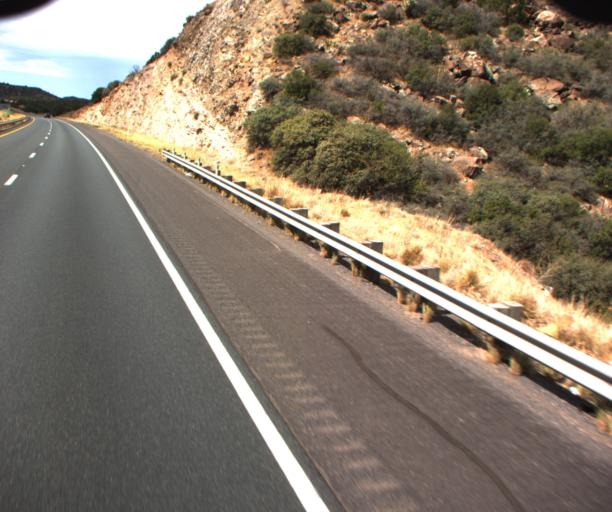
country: US
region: Arizona
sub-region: Yavapai County
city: Camp Verde
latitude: 34.5003
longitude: -112.0034
